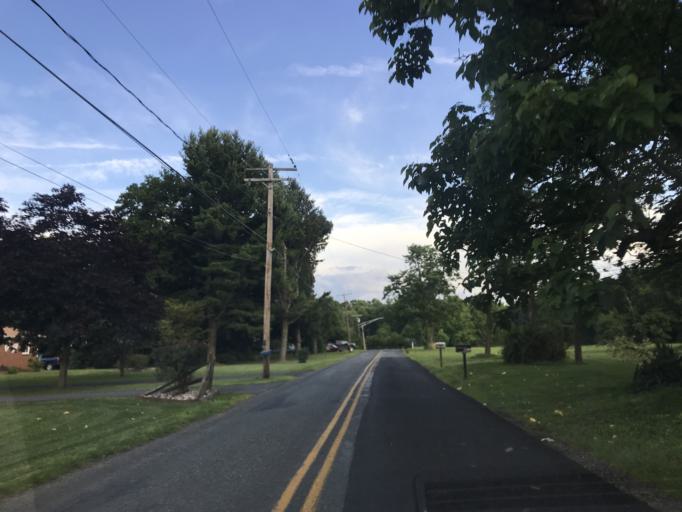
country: US
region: Maryland
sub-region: Harford County
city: Aberdeen
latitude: 39.5288
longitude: -76.2177
